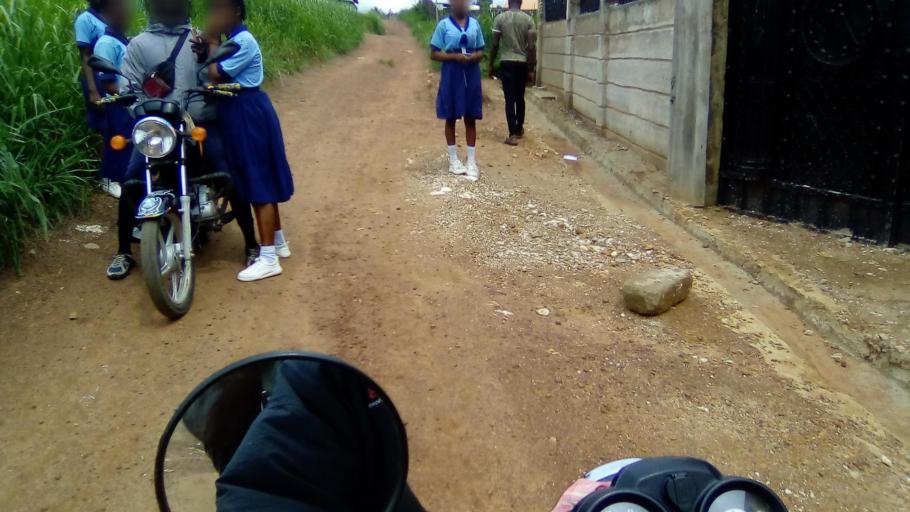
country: SL
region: Southern Province
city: Bo
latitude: 7.9354
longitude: -11.7225
